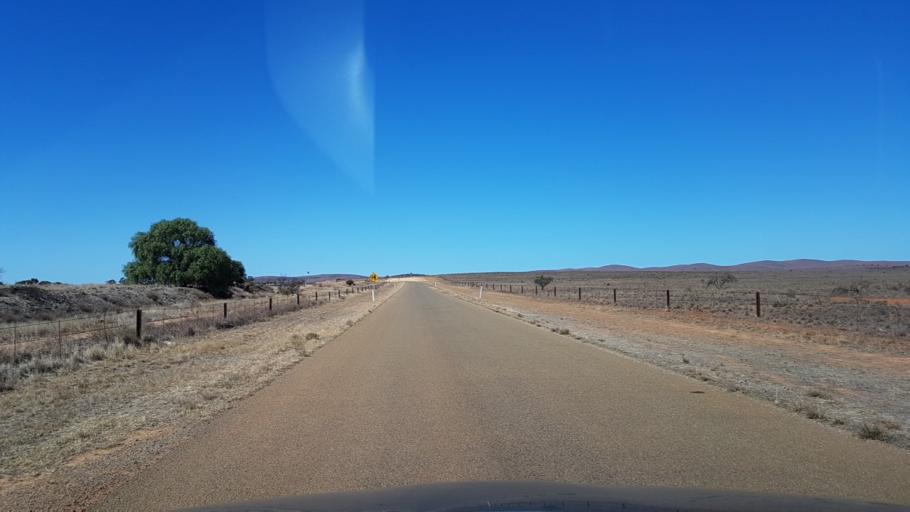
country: AU
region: South Australia
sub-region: Peterborough
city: Peterborough
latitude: -32.9727
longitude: 138.8553
